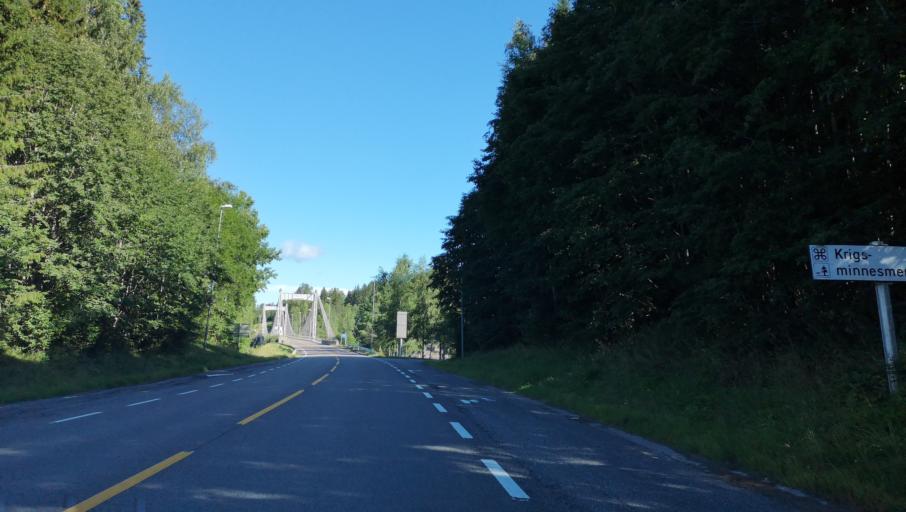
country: NO
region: Ostfold
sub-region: Spydeberg
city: Spydeberg
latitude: 59.6010
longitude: 11.1031
